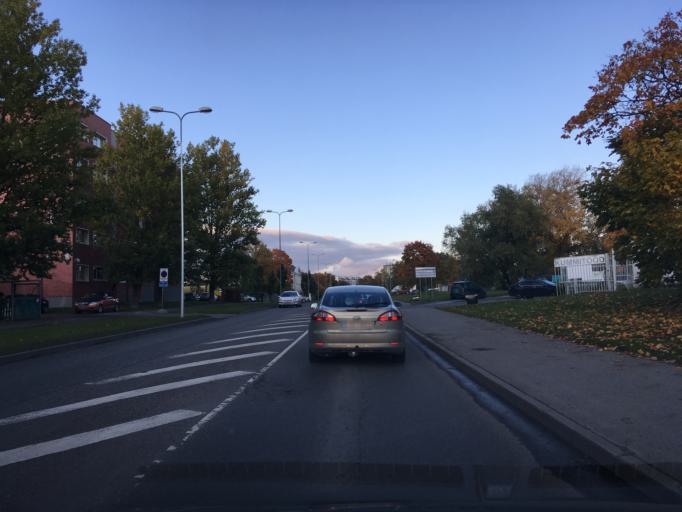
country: EE
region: Harju
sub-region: Tallinna linn
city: Tallinn
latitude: 59.4306
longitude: 24.8081
